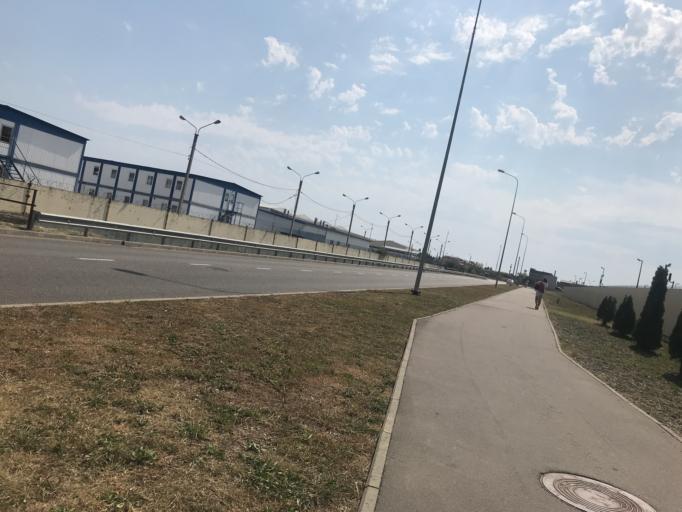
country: RU
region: Krasnodarskiy
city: Vysokoye
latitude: 43.3998
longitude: 39.9844
